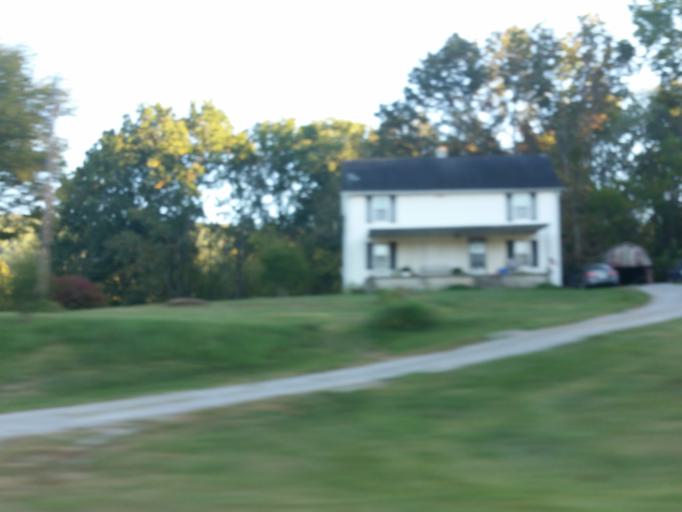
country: US
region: Tennessee
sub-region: Grainger County
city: Rutledge
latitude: 36.3142
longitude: -83.5418
